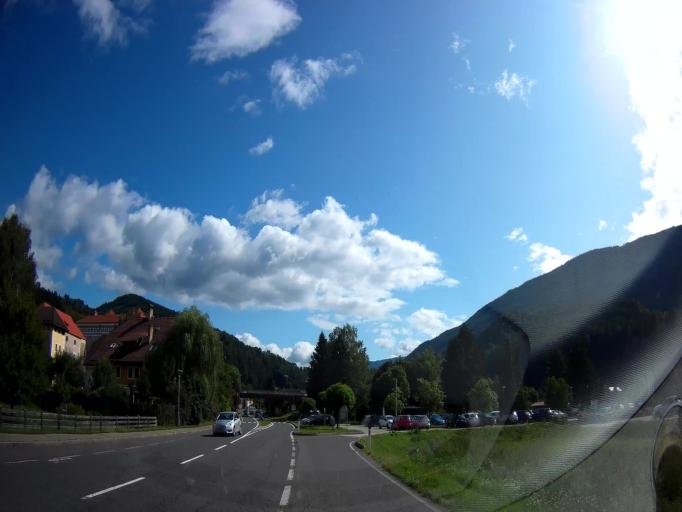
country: AT
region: Carinthia
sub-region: Politischer Bezirk Spittal an der Drau
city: Gmuend
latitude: 46.9054
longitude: 13.5358
